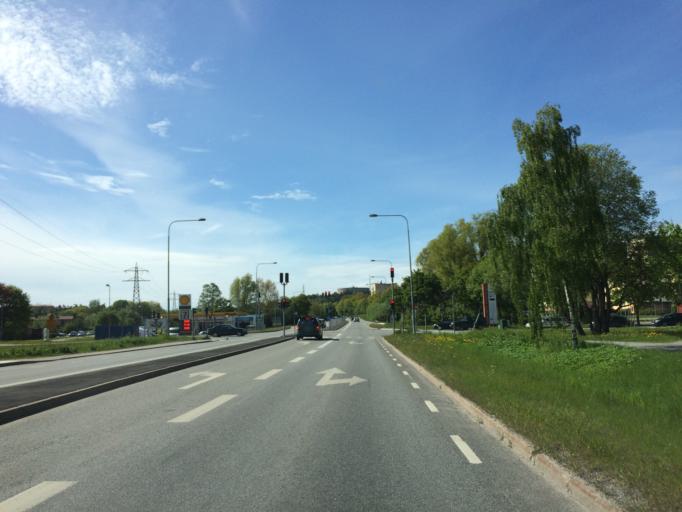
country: SE
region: Stockholm
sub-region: Sollentuna Kommun
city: Sollentuna
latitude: 59.4431
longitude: 17.9672
